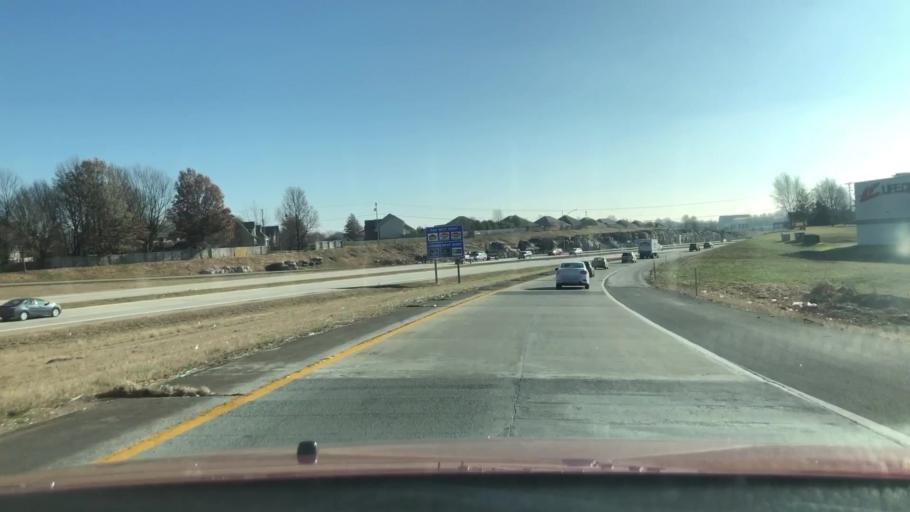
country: US
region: Missouri
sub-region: Greene County
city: Battlefield
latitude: 37.1414
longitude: -93.3171
